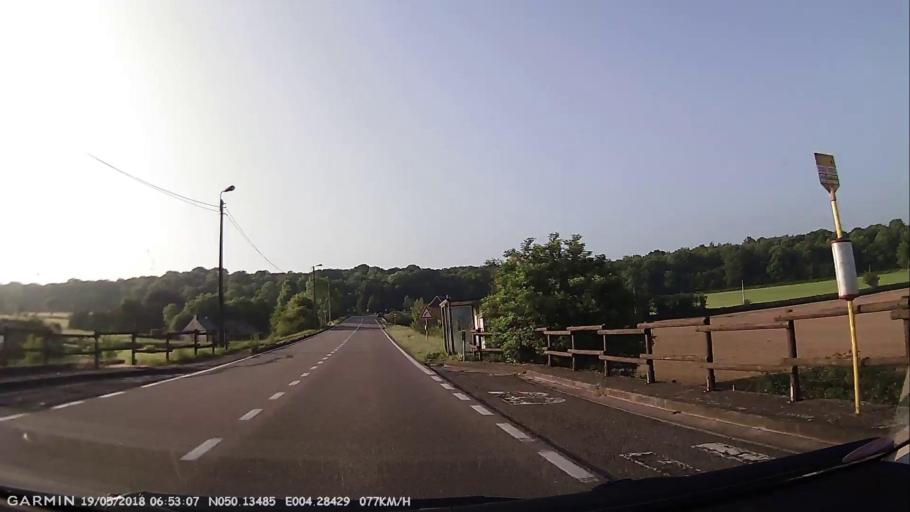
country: BE
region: Wallonia
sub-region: Province du Hainaut
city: Froidchapelle
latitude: 50.1346
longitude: 4.2845
